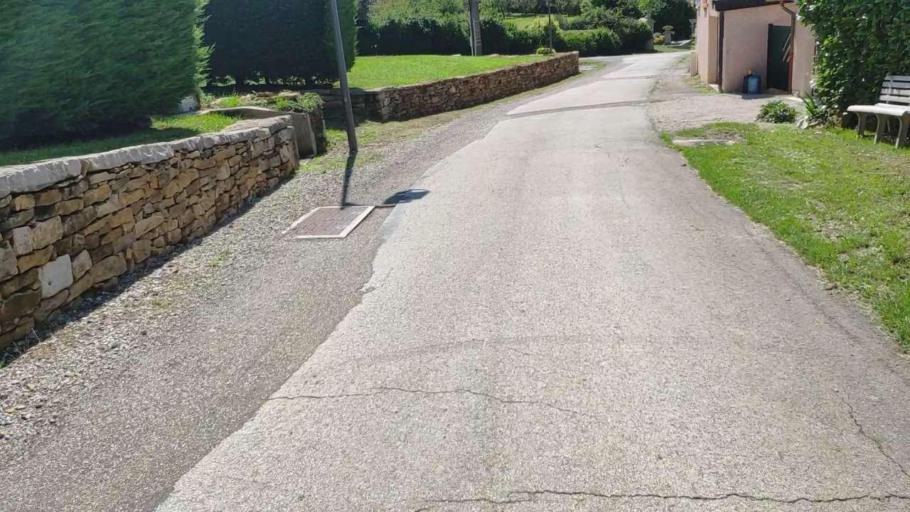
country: FR
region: Franche-Comte
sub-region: Departement du Jura
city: Bletterans
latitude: 46.8021
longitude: 5.5617
